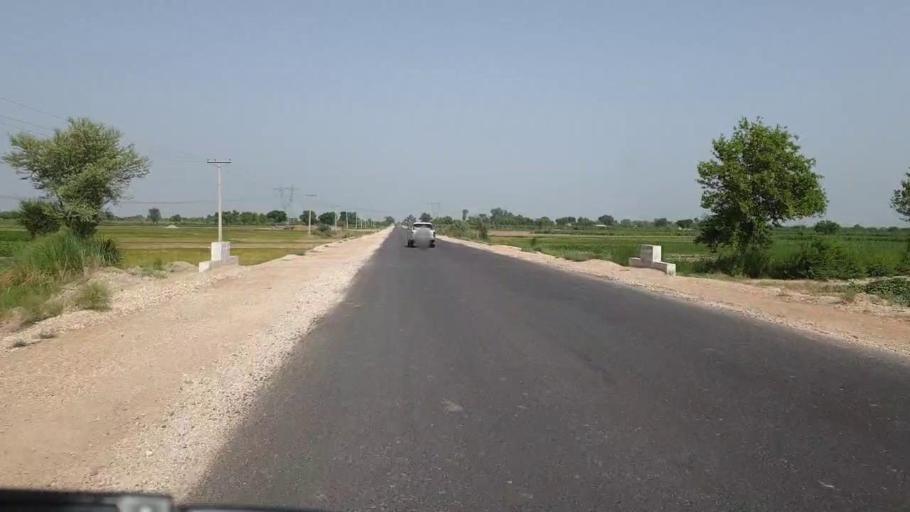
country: PK
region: Sindh
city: Sakrand
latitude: 26.2564
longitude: 68.1948
